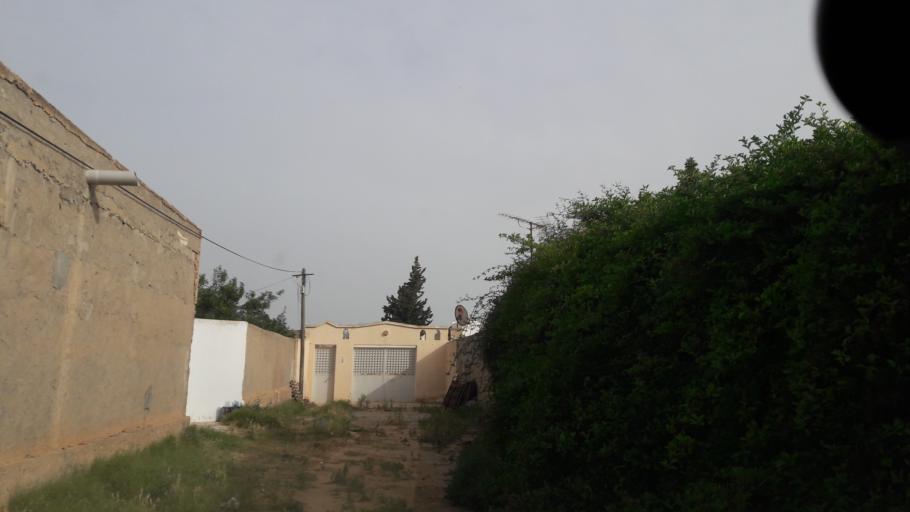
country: TN
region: Safaqis
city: Al Qarmadah
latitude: 34.7781
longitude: 10.7682
